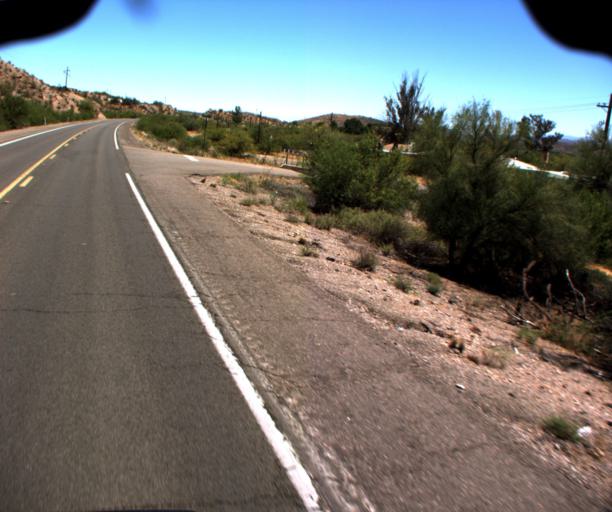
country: US
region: Arizona
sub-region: Pinal County
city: Kearny
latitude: 32.9649
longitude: -110.7543
